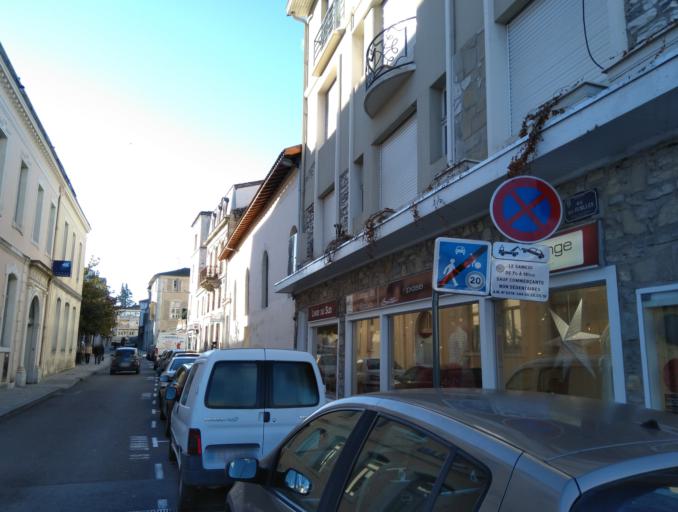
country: FR
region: Aquitaine
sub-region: Departement des Landes
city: Dax
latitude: 43.7106
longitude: -1.0514
